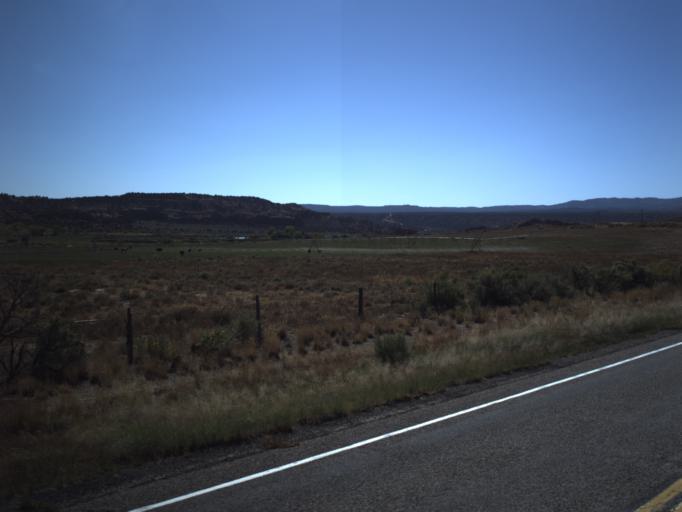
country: US
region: Utah
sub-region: Garfield County
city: Panguitch
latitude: 37.5625
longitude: -112.0114
